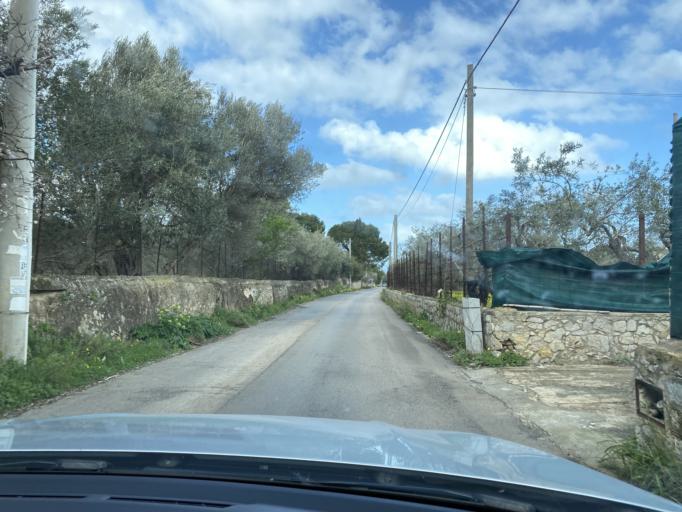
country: IT
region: Sicily
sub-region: Palermo
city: Carini
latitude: 38.1531
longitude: 13.1676
